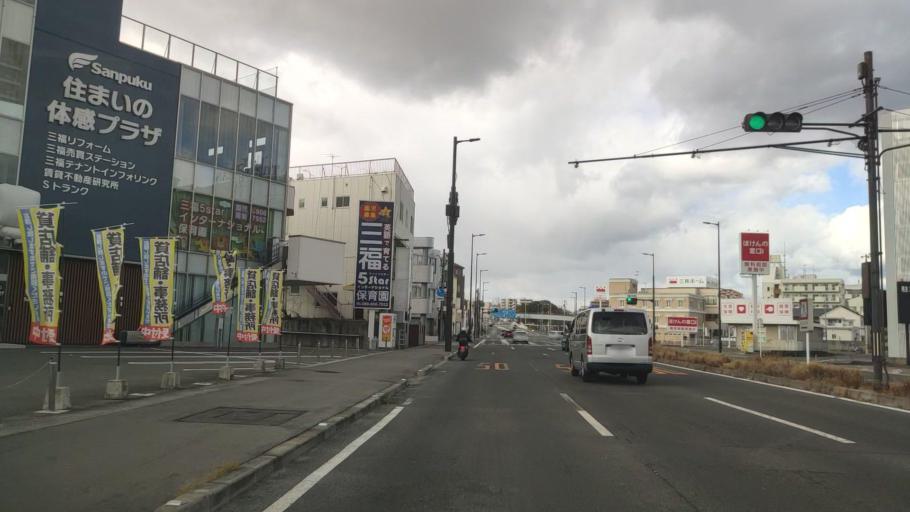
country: JP
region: Ehime
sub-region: Shikoku-chuo Shi
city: Matsuyama
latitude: 33.8318
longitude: 132.7791
